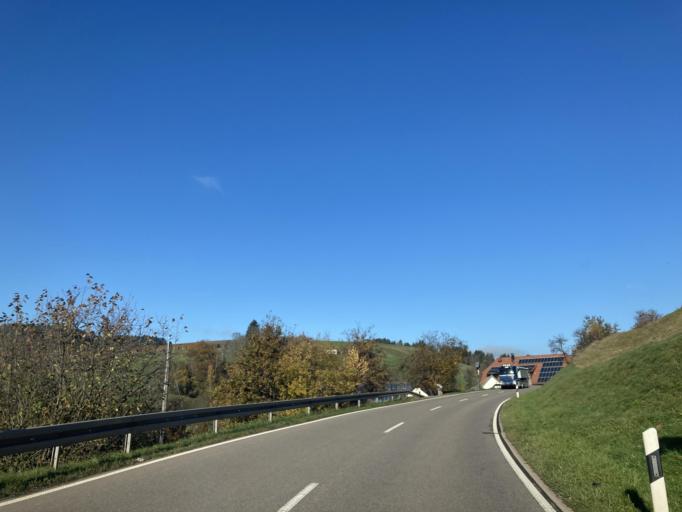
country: DE
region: Baden-Wuerttemberg
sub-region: Freiburg Region
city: Elzach
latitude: 48.1958
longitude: 8.0827
